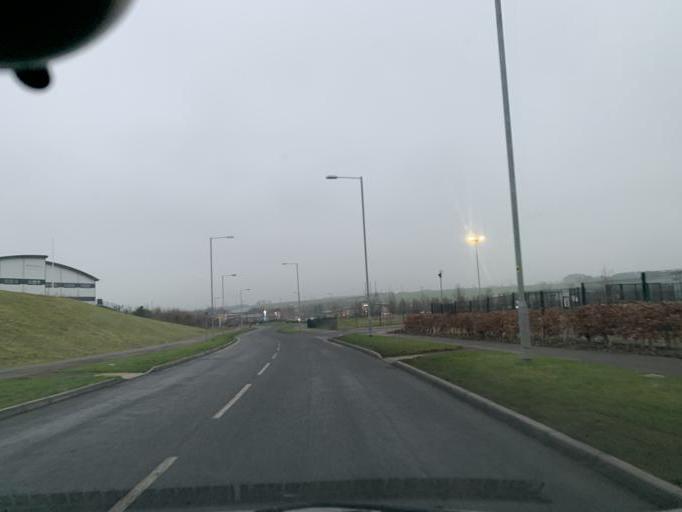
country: GB
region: England
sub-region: Wiltshire
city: Bulford
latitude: 51.1750
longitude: -1.7566
